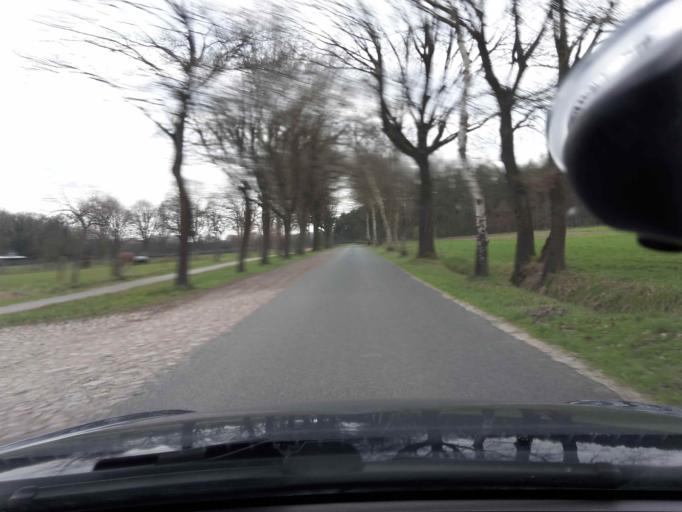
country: DE
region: Lower Saxony
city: Buchholz in der Nordheide
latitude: 53.2793
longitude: 9.8994
